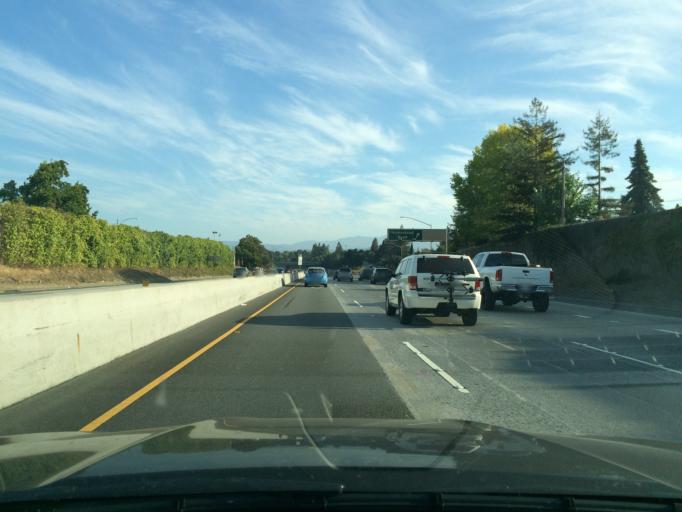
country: US
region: California
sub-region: Santa Clara County
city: Cupertino
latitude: 37.3425
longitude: -122.0599
